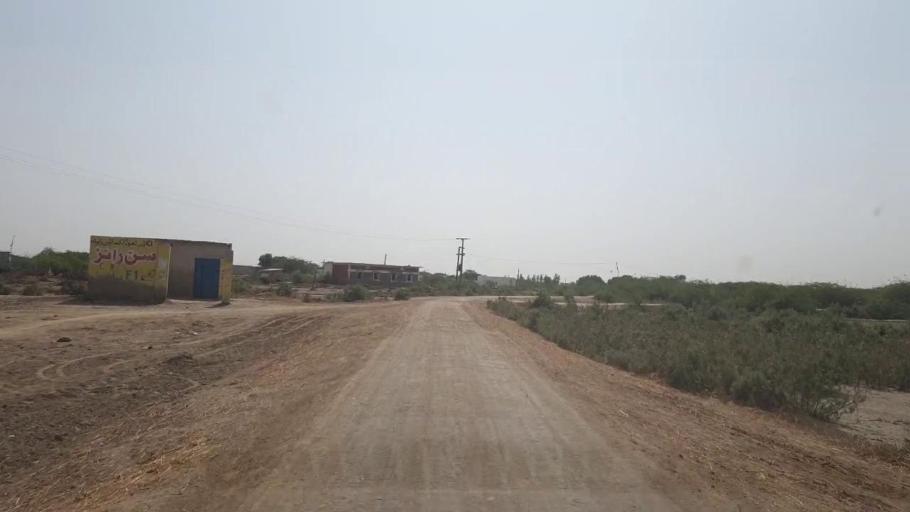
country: PK
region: Sindh
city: Jati
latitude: 24.4692
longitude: 68.5567
